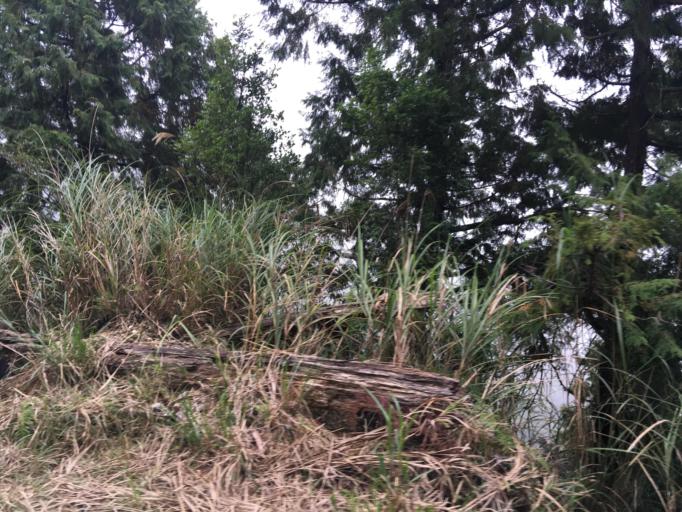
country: TW
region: Taiwan
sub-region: Yilan
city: Yilan
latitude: 24.4819
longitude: 121.5359
